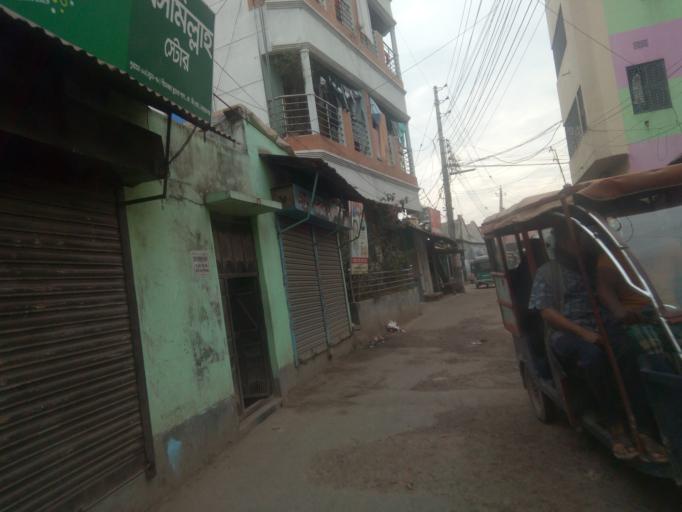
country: BD
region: Dhaka
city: Narayanganj
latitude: 23.6009
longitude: 90.5024
